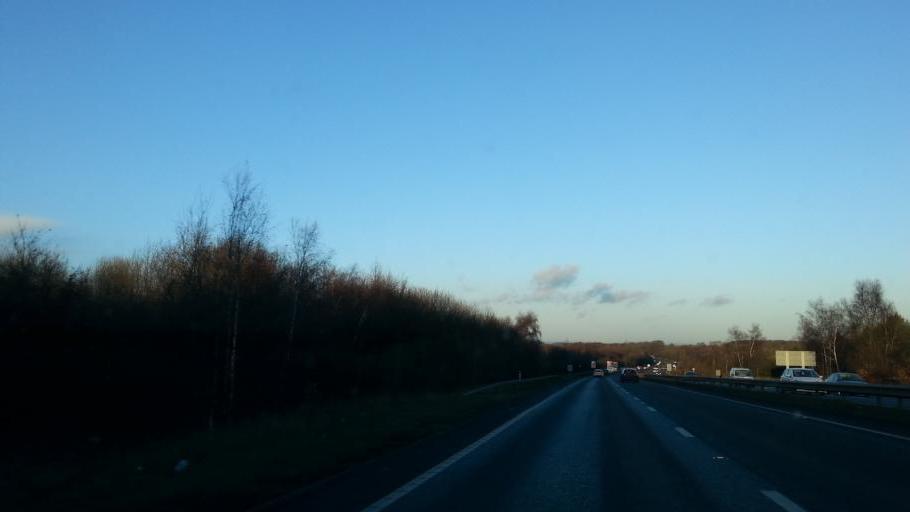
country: GB
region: England
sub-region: Leicestershire
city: Ashby de la Zouch
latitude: 52.7625
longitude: -1.4329
